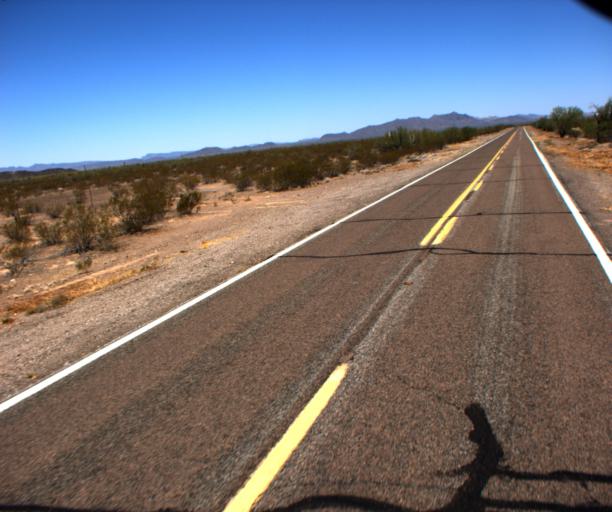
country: US
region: Arizona
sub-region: Pima County
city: Ajo
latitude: 32.2347
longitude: -112.7170
